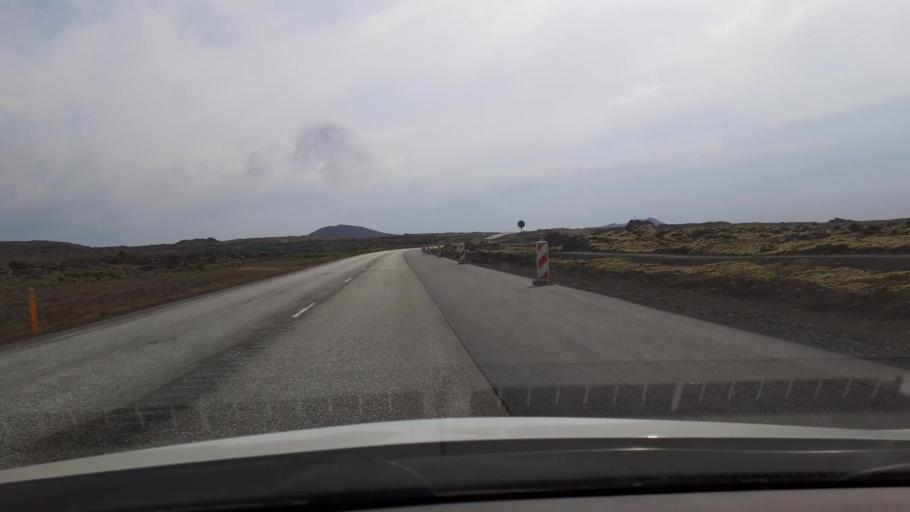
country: IS
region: Southern Peninsula
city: Grindavik
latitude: 63.9126
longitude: -22.4205
